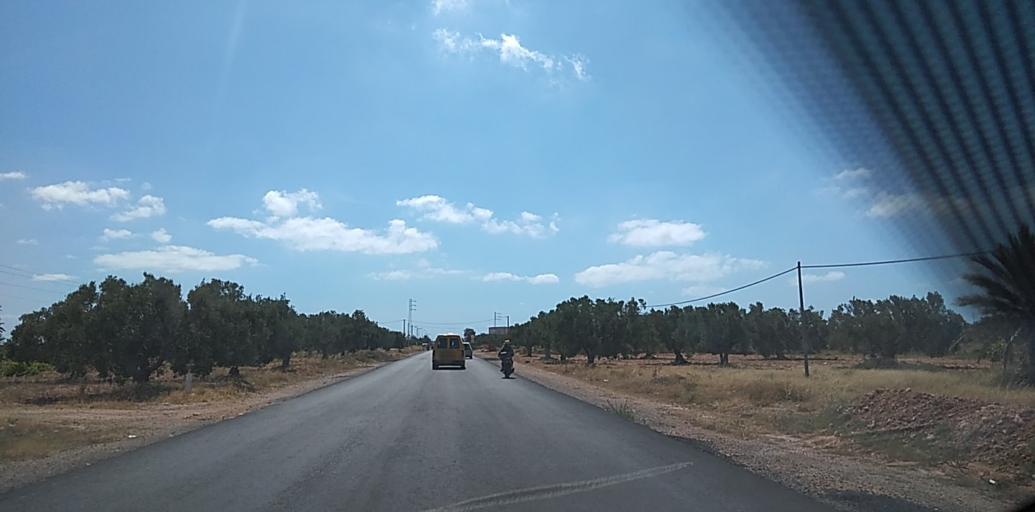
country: TN
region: Safaqis
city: Al Qarmadah
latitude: 34.6572
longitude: 11.0849
